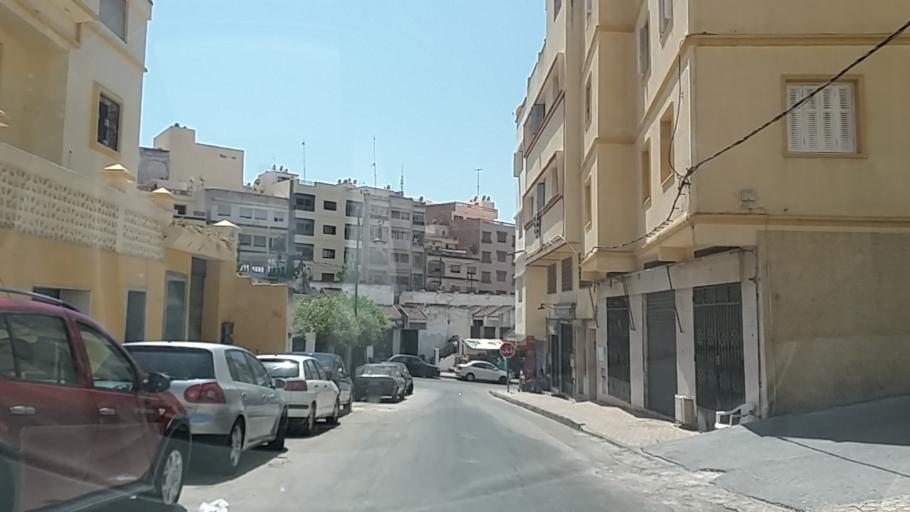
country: MA
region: Tanger-Tetouan
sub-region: Tanger-Assilah
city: Tangier
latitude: 35.7860
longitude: -5.8244
